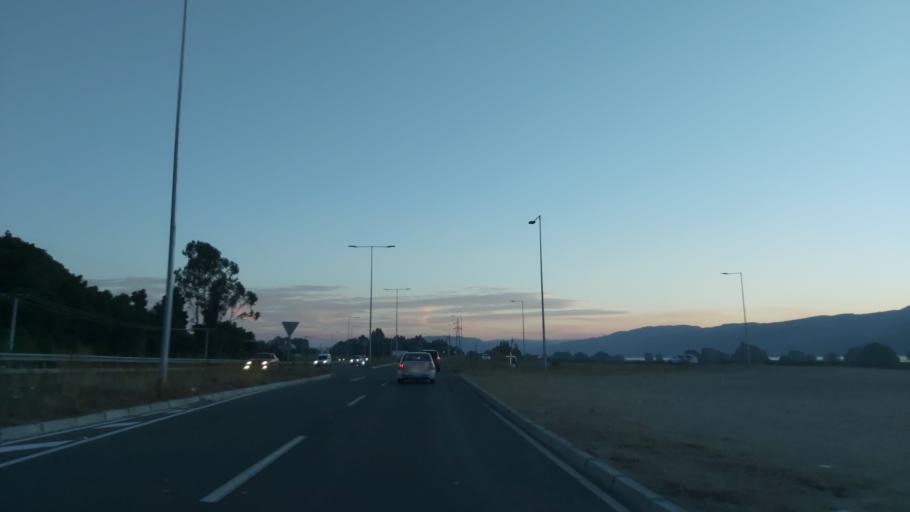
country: CL
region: Biobio
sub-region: Provincia de Concepcion
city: Chiguayante
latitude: -36.8904
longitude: -73.0369
